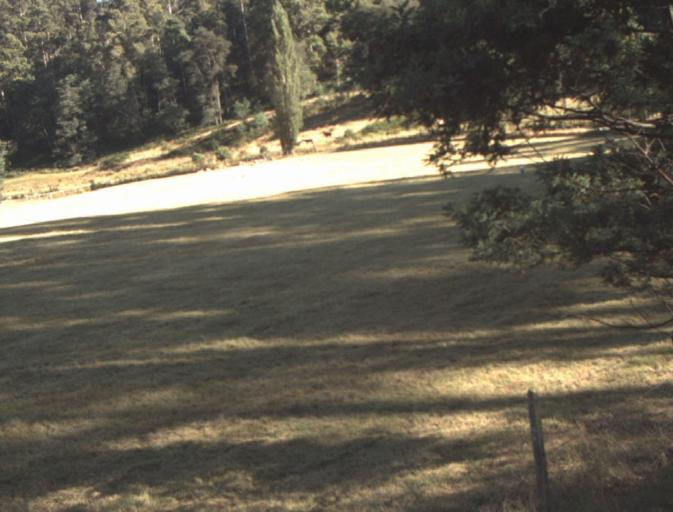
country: AU
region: Tasmania
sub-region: Launceston
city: Mayfield
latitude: -41.2886
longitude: 147.1972
